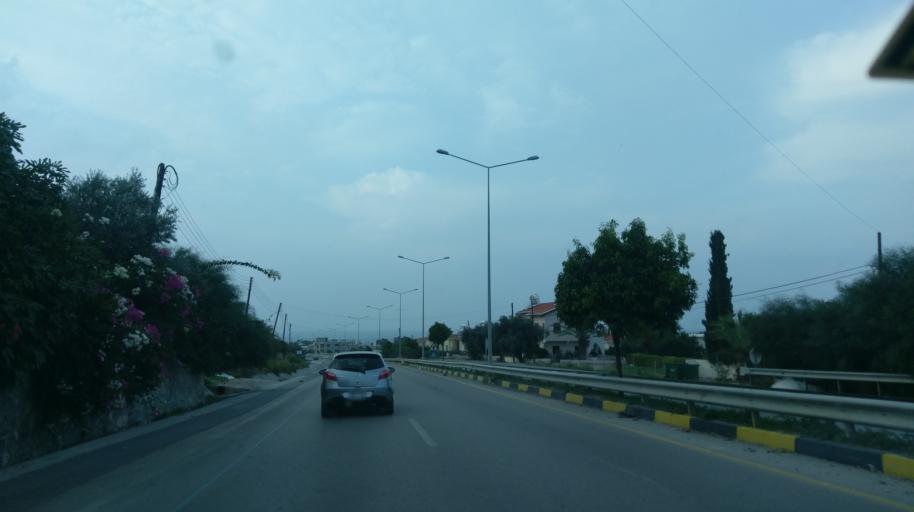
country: CY
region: Keryneia
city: Kyrenia
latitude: 35.3373
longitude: 33.2567
